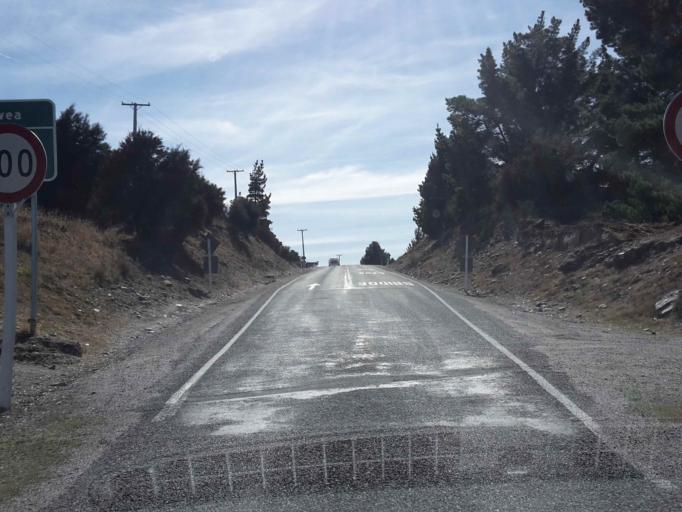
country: NZ
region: Otago
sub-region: Queenstown-Lakes District
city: Wanaka
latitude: -44.7304
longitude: 169.2818
